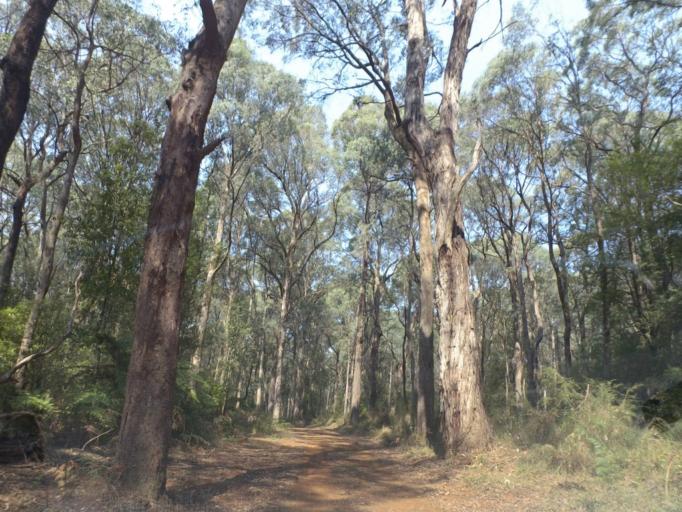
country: AU
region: Victoria
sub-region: Yarra Ranges
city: Healesville
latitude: -37.5832
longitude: 145.6674
